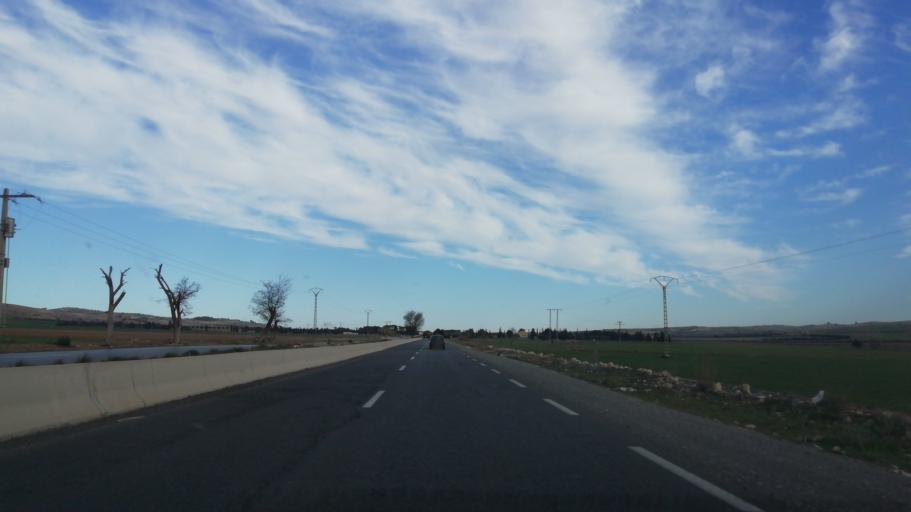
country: DZ
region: Sidi Bel Abbes
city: Sfizef
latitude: 35.1849
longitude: -0.3905
